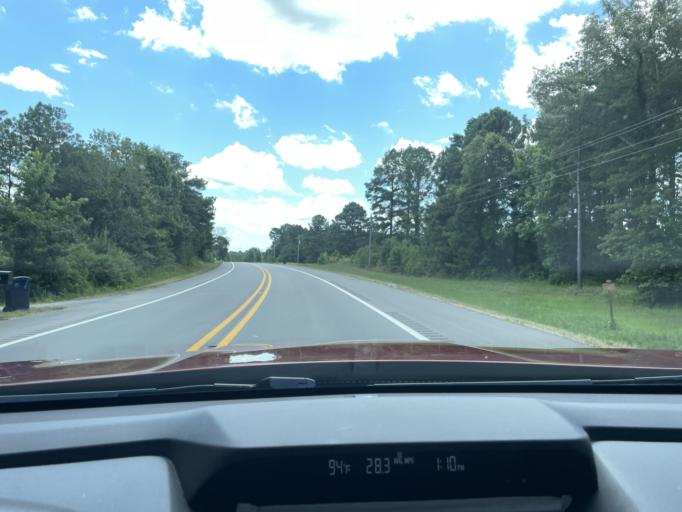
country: US
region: Arkansas
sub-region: Drew County
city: Monticello
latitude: 33.7141
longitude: -91.8109
